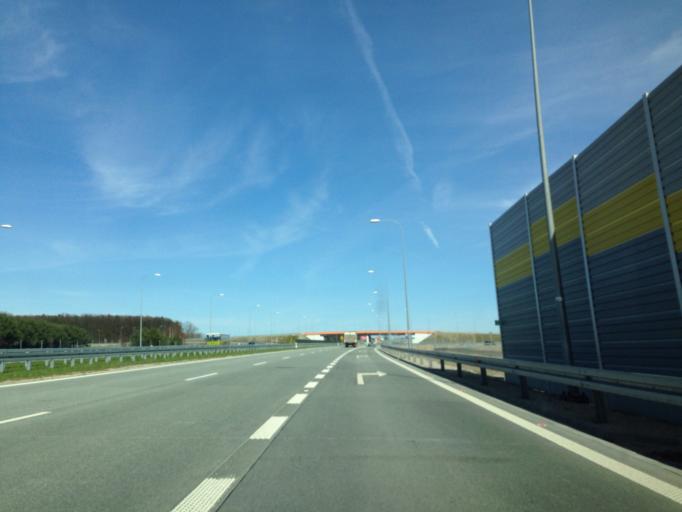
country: PL
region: Lodz Voivodeship
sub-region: Powiat zdunskowolski
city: Zapolice
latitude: 51.5914
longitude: 18.8181
